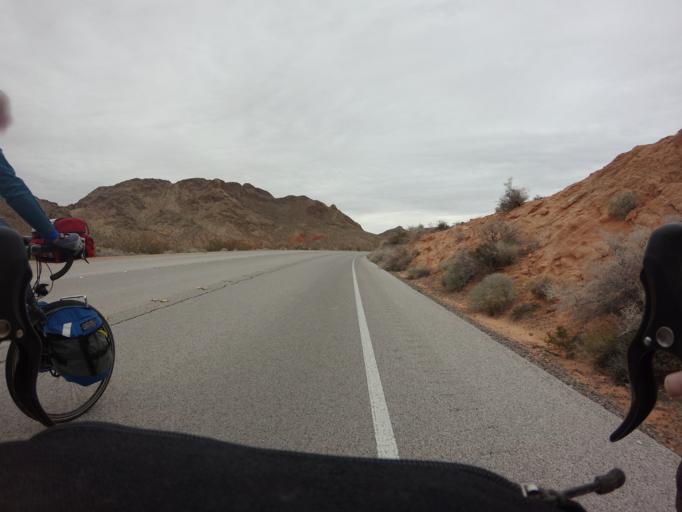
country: US
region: Nevada
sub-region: Clark County
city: Moapa Valley
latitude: 36.2437
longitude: -114.5143
